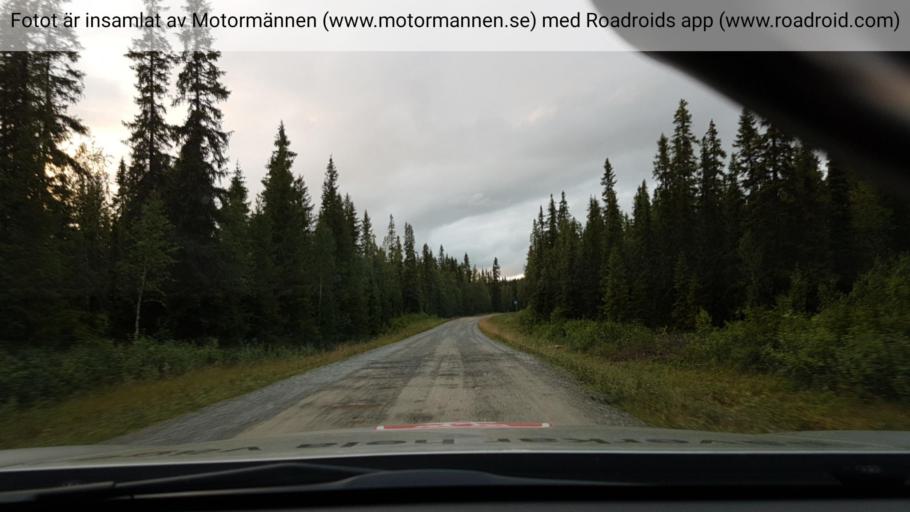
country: SE
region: Vaesterbotten
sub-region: Vilhelmina Kommun
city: Sjoberg
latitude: 65.5274
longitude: 15.4384
